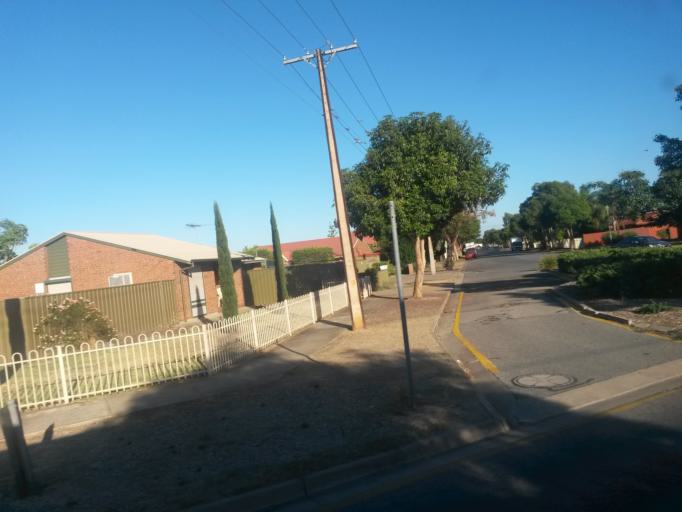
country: AU
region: South Australia
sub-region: Prospect
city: Prospect
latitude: -34.8889
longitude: 138.5761
